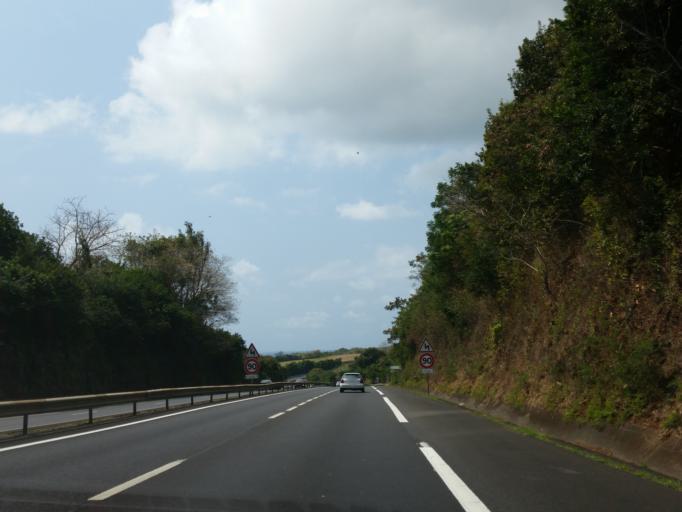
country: RE
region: Reunion
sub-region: Reunion
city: Sainte-Marie
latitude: -20.8981
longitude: 55.5710
